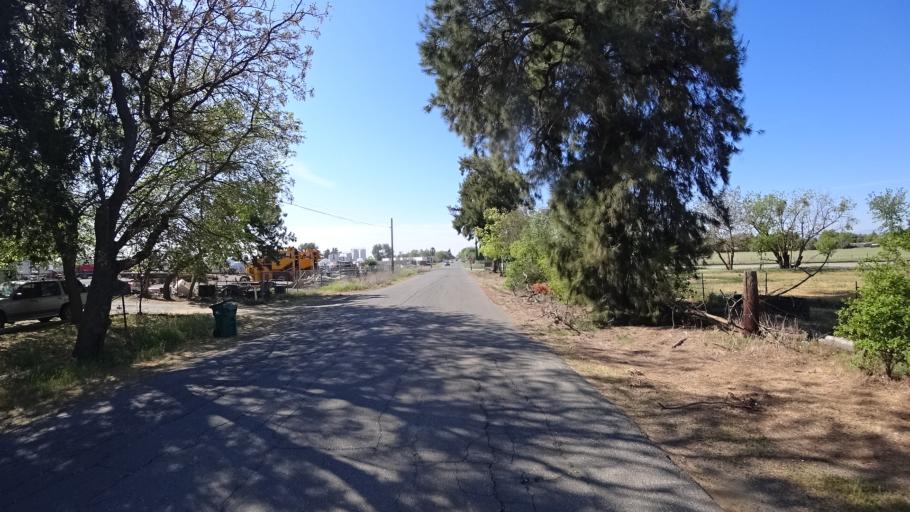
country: US
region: California
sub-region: Glenn County
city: Willows
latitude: 39.5308
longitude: -122.1955
